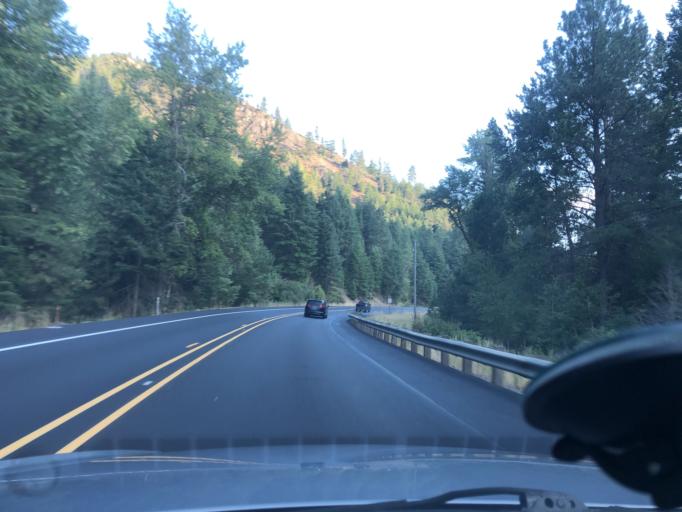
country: US
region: Washington
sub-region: Kittitas County
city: Cle Elum
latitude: 47.2276
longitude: -120.6956
